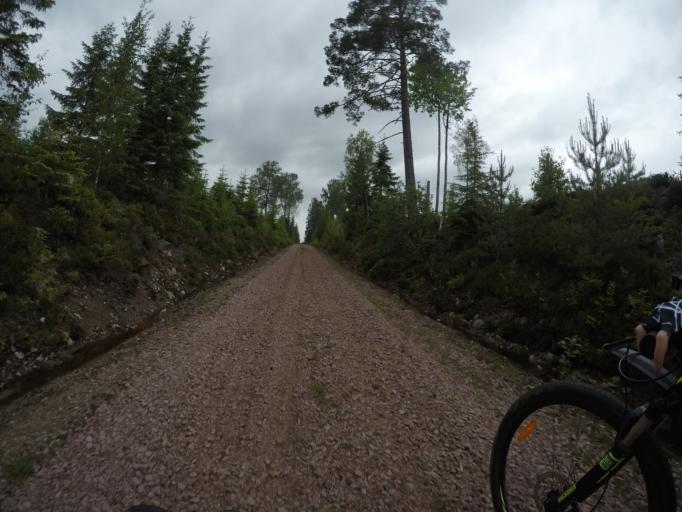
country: SE
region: OErebro
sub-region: Hallefors Kommun
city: Haellefors
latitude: 60.0214
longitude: 14.5797
